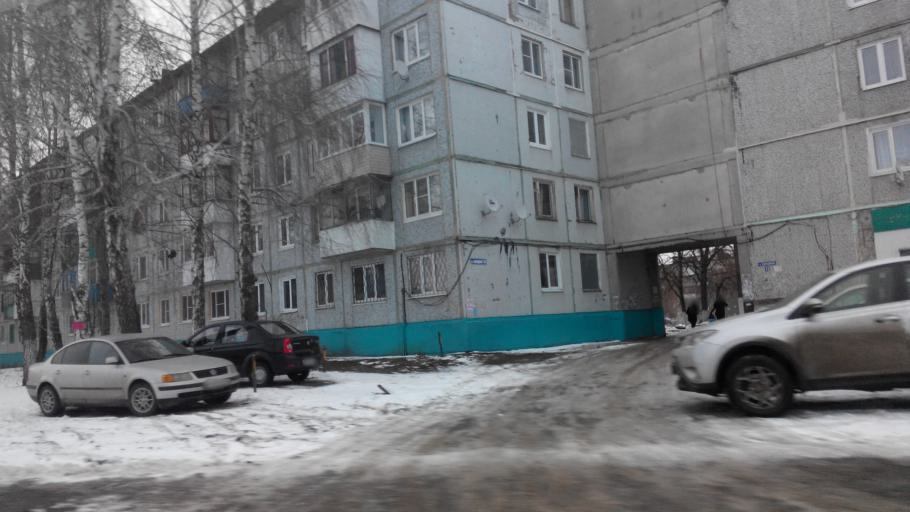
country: RU
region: Tula
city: Podlesnyy
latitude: 53.9665
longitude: 38.2873
